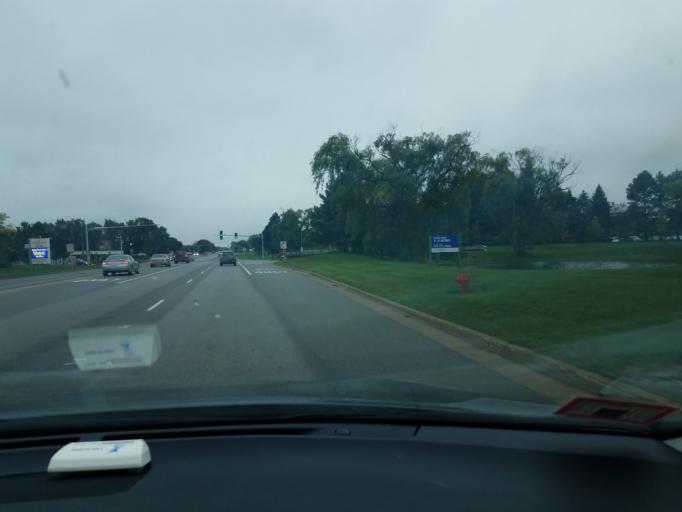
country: US
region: Illinois
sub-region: Lake County
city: Lincolnshire
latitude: 42.1957
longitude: -87.9311
